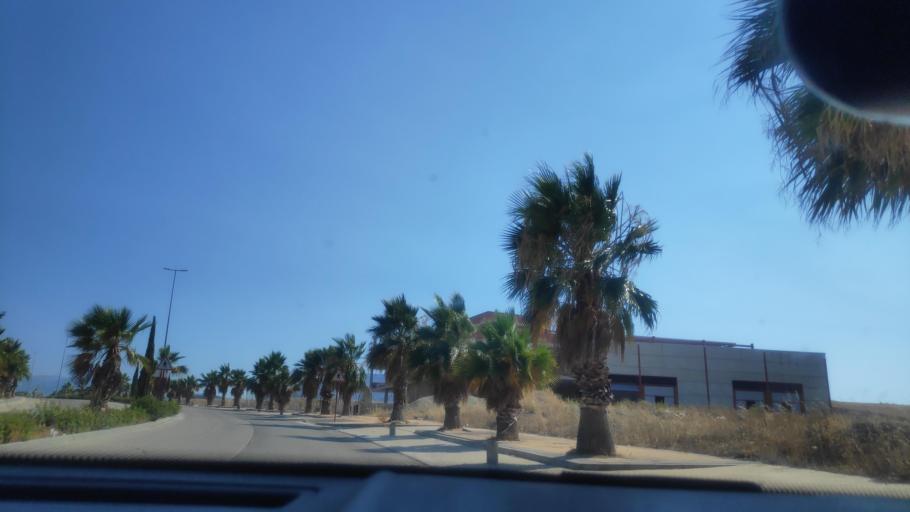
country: ES
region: Andalusia
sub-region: Provincia de Jaen
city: Jaen
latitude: 37.8266
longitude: -3.7761
